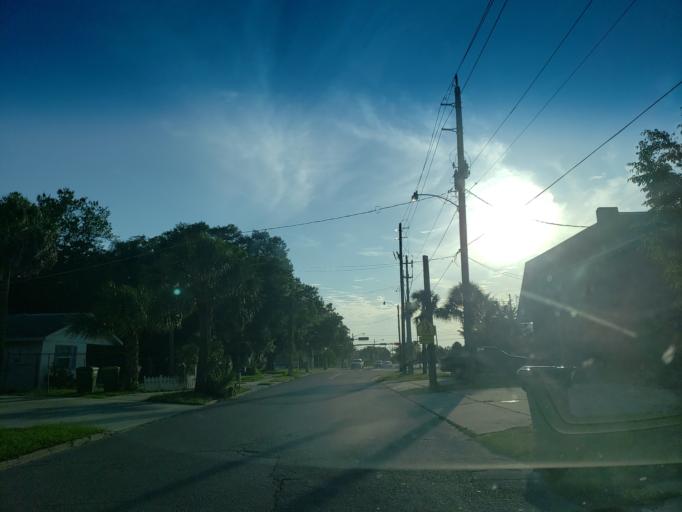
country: US
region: Florida
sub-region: Sarasota County
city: Sarasota
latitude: 27.3445
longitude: -82.5374
